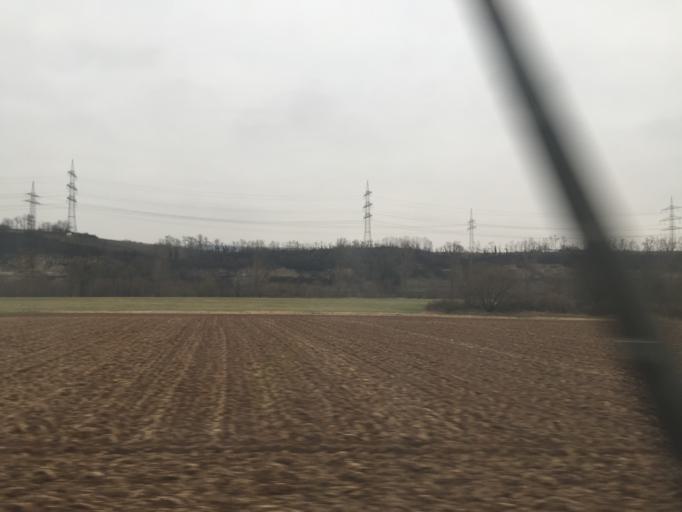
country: DE
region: Baden-Wuerttemberg
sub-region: Regierungsbezirk Stuttgart
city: Talheim
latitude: 49.0855
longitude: 9.1733
